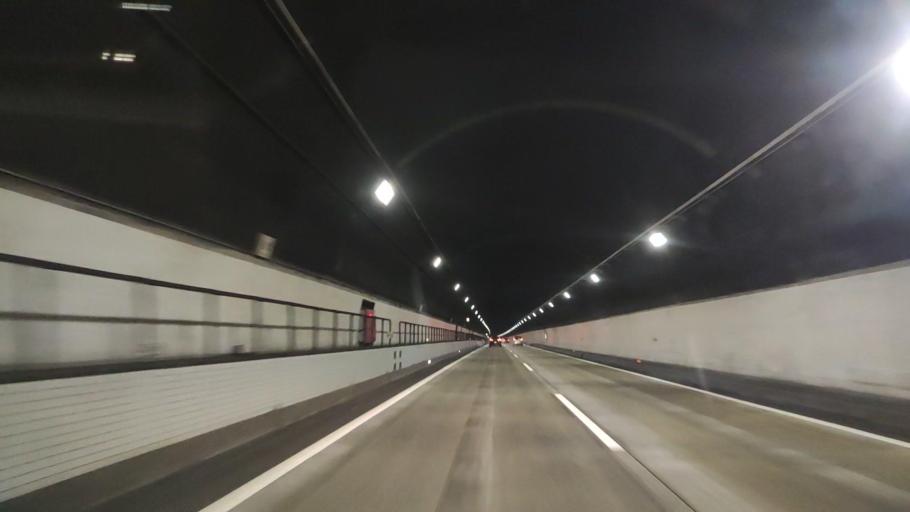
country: JP
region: Hiroshima
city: Shin'ichi
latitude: 34.4760
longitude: 133.2771
